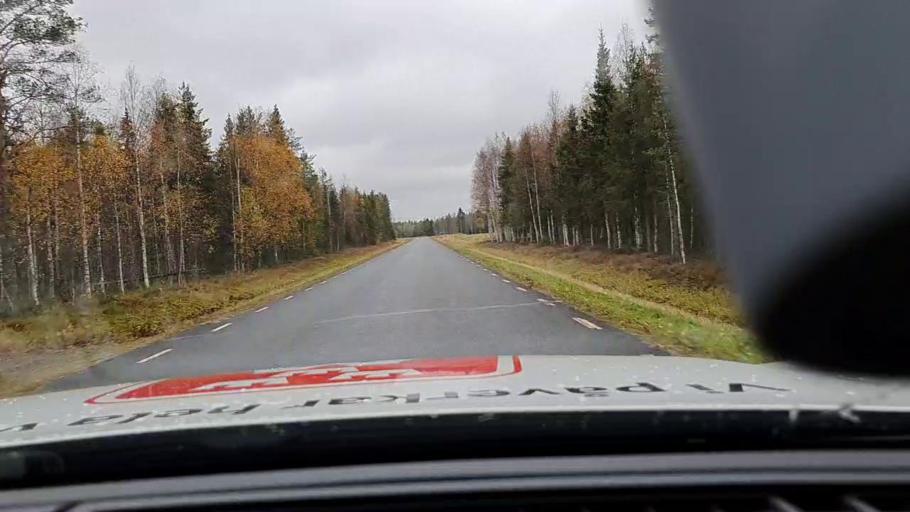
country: SE
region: Norrbotten
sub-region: Haparanda Kommun
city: Haparanda
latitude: 65.9297
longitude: 23.8171
